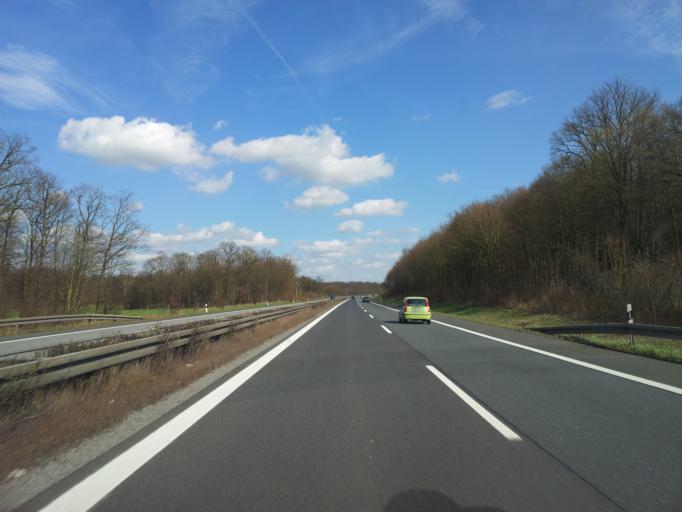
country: DE
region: Bavaria
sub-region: Regierungsbezirk Unterfranken
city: Wonfurt
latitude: 50.0057
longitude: 10.4790
